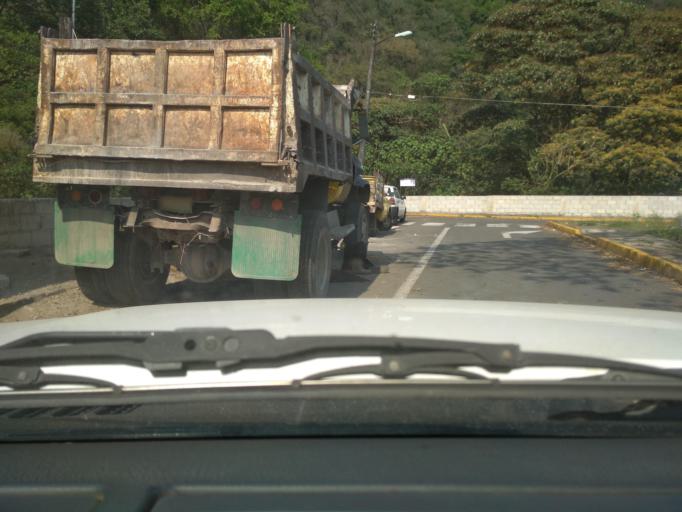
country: MX
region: Veracruz
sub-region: Mariano Escobedo
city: Palmira
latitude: 18.8726
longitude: -97.0949
